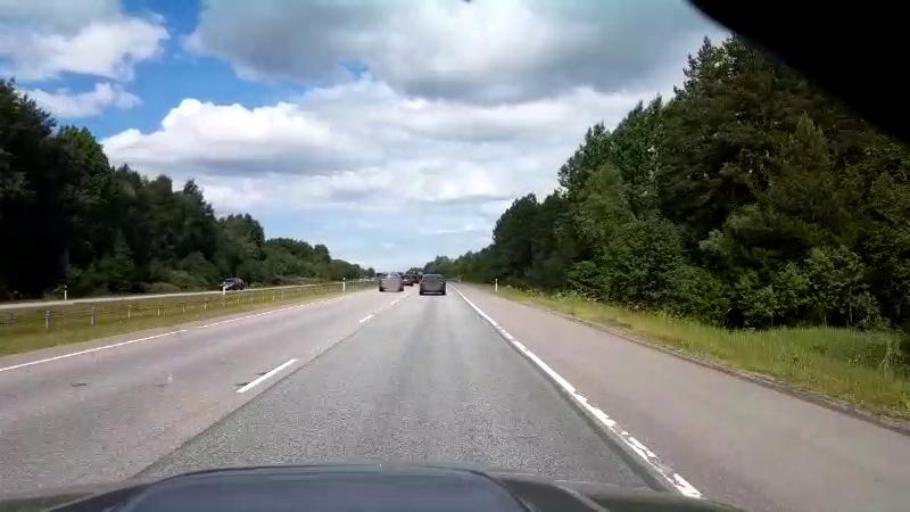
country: EE
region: Harju
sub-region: Saue linn
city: Saue
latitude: 59.2633
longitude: 24.5126
